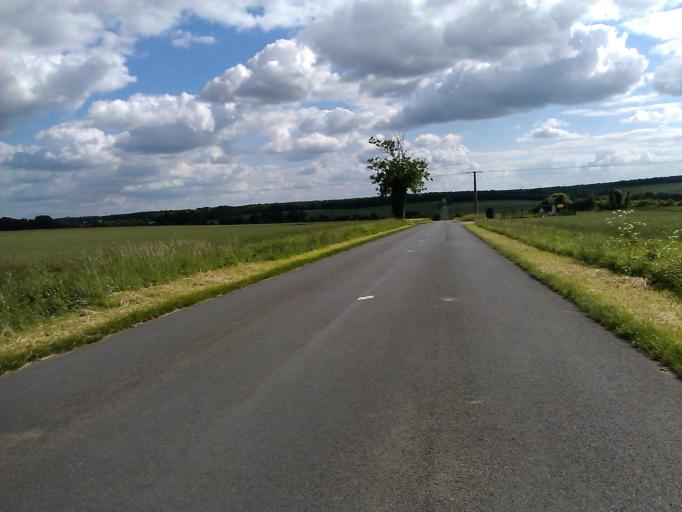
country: FR
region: Poitou-Charentes
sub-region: Departement de la Charente
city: Mansle
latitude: 45.8649
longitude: 0.1706
